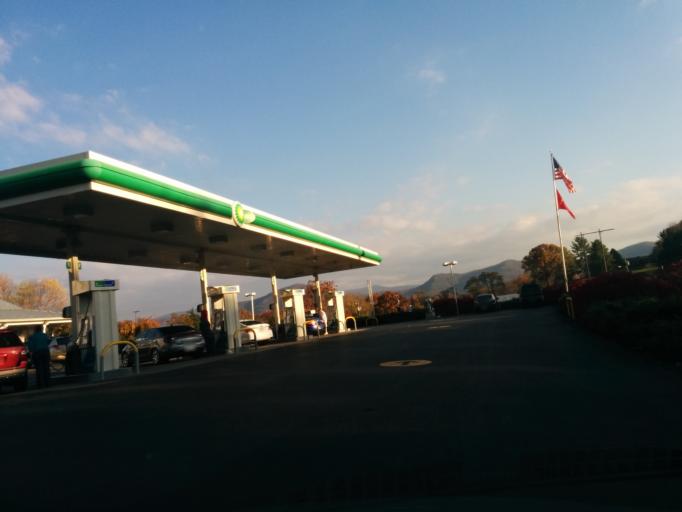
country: US
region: Virginia
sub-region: City of Buena Vista
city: Buena Vista
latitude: 37.8842
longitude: -79.2837
